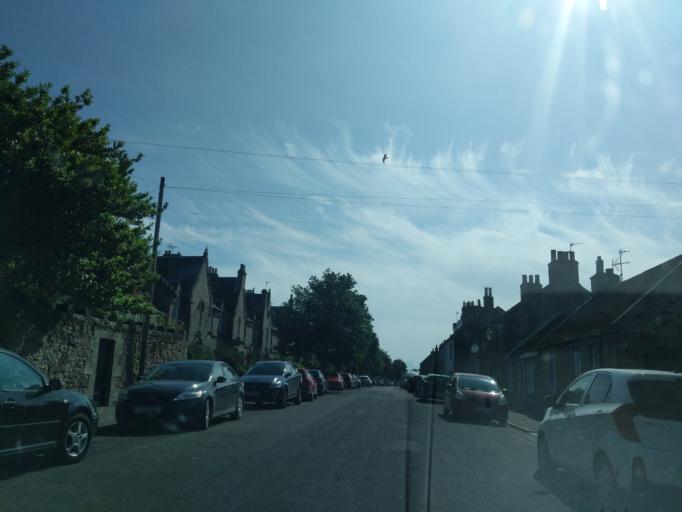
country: GB
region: Scotland
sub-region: Fife
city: Anstruther
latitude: 56.2611
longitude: -2.6229
